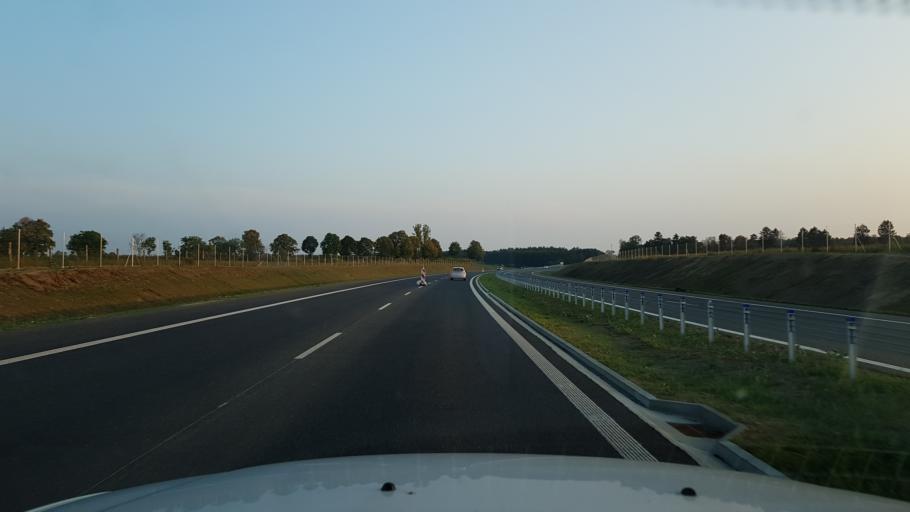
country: PL
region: West Pomeranian Voivodeship
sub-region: Powiat gryficki
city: Ploty
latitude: 53.7674
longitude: 15.2358
